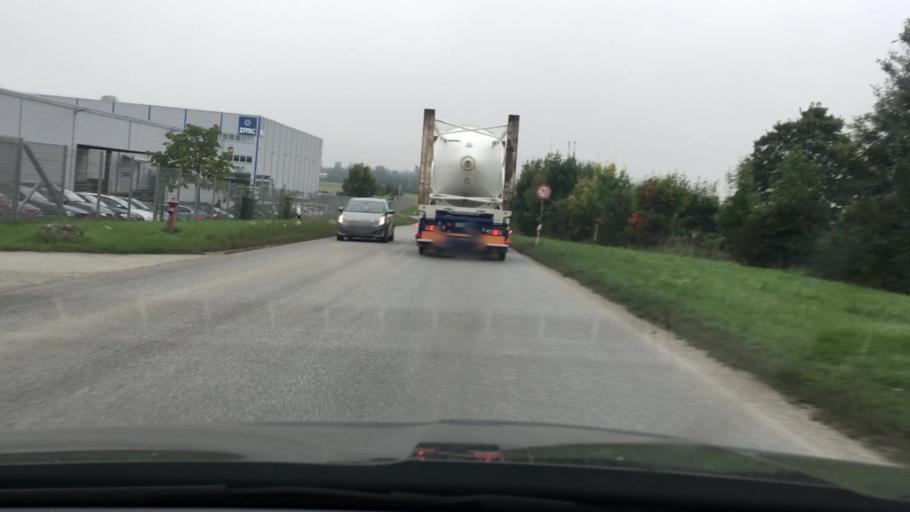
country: DE
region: Bavaria
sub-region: Lower Bavaria
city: Plattling
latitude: 48.7985
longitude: 12.8830
